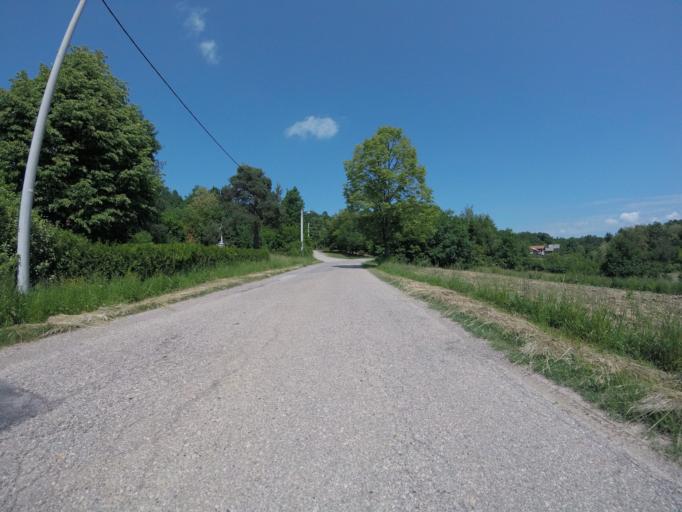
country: HR
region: Grad Zagreb
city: Strmec
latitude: 45.5786
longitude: 15.9434
